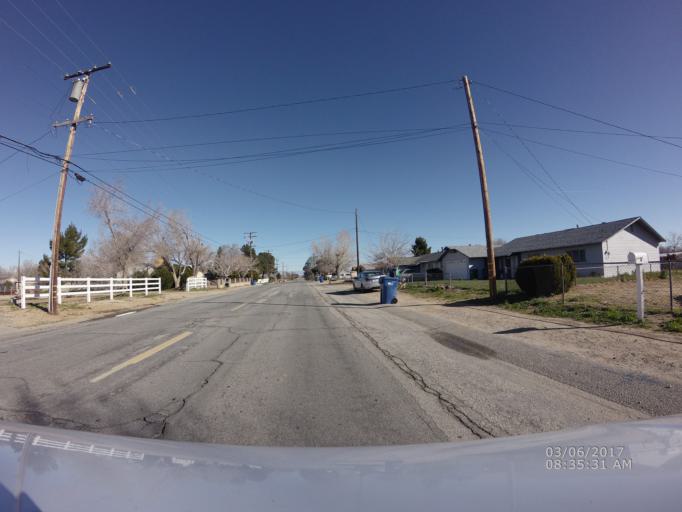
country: US
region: California
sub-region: Los Angeles County
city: Quartz Hill
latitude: 34.6538
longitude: -118.2100
